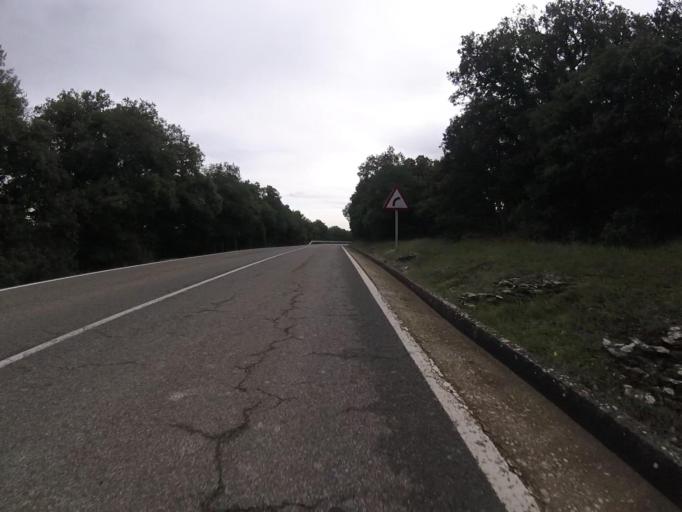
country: ES
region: Navarre
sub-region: Provincia de Navarra
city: Lezaun
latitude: 42.7508
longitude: -2.0148
